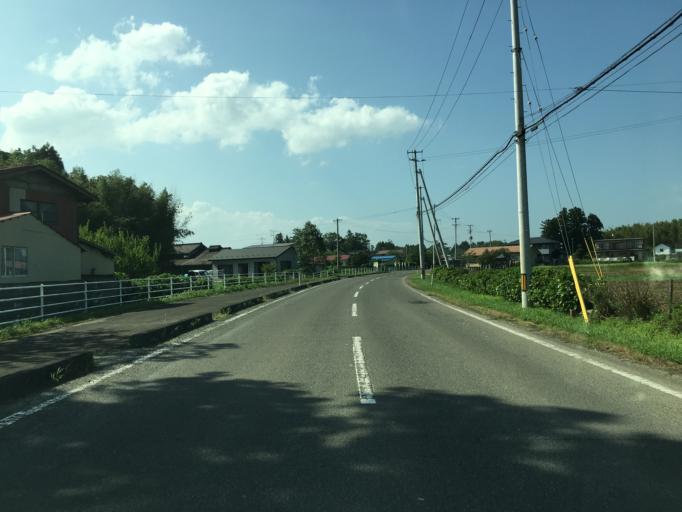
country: JP
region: Miyagi
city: Kakuda
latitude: 37.9481
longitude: 140.7973
